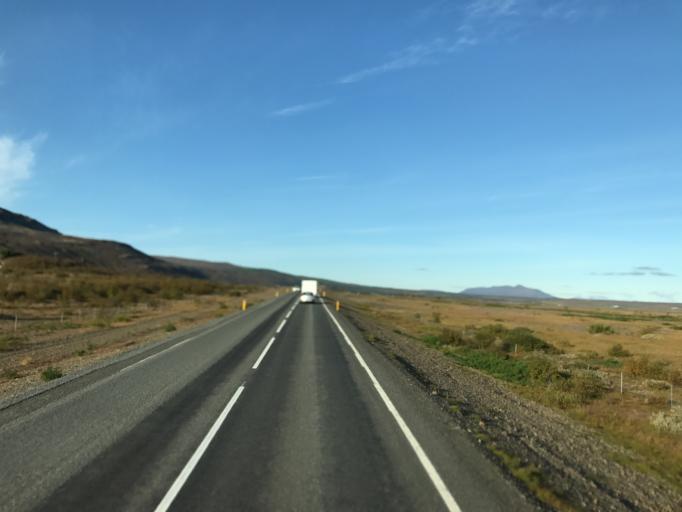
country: IS
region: South
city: Selfoss
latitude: 64.2818
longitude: -20.3441
